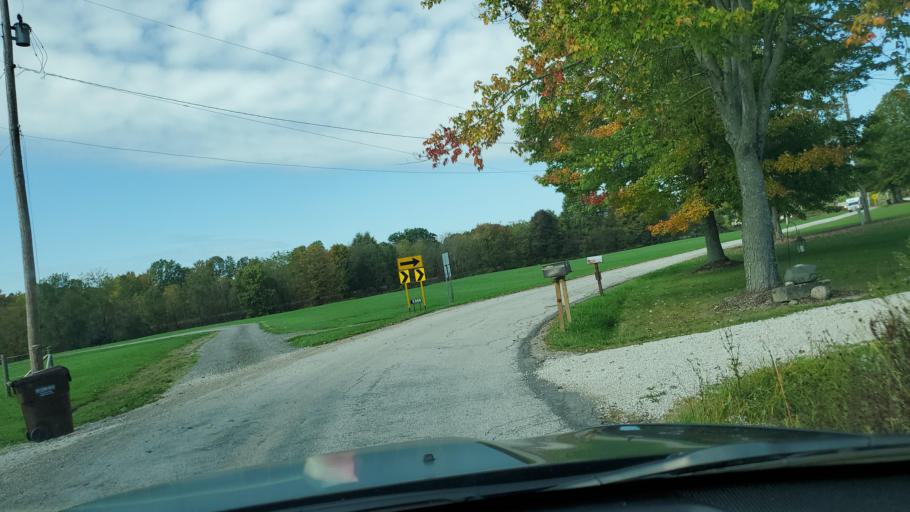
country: US
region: Ohio
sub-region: Trumbull County
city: Cortland
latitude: 41.4054
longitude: -80.6271
